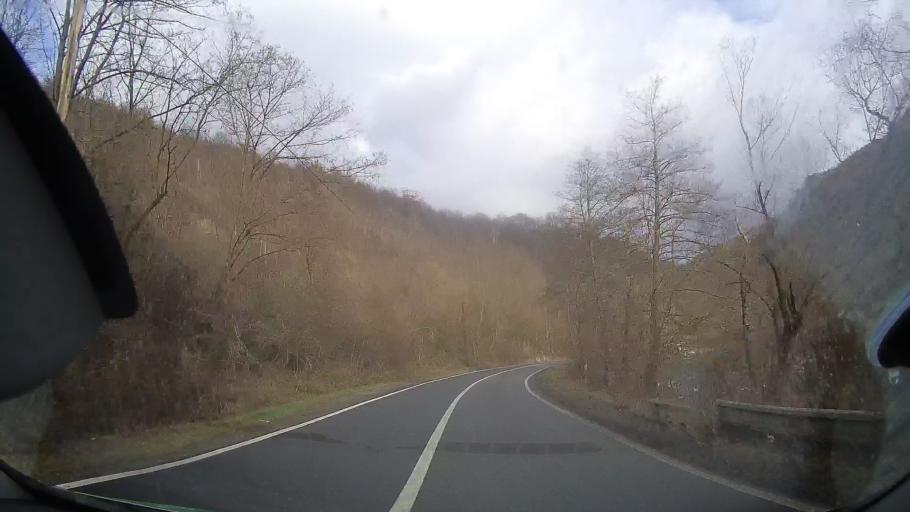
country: RO
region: Alba
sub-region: Comuna Rimetea
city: Rimetea
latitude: 46.4876
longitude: 23.5254
